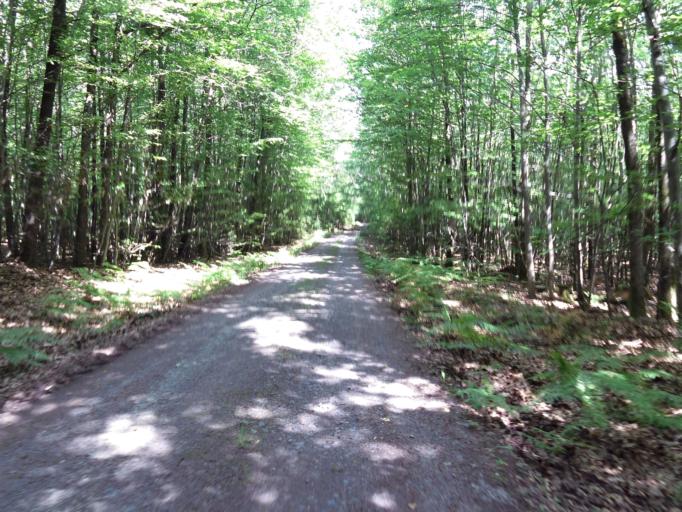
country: DE
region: Rheinland-Pfalz
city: Waldleiningen
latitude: 49.3904
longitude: 7.9117
